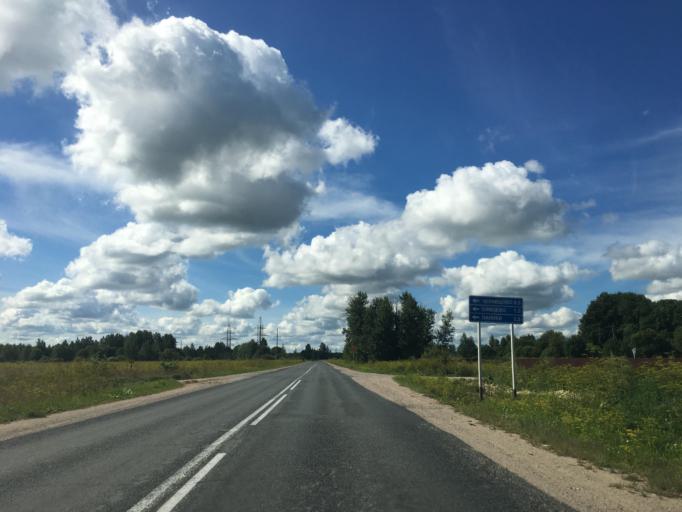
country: RU
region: Pskov
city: Pskov
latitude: 57.7779
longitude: 28.1669
